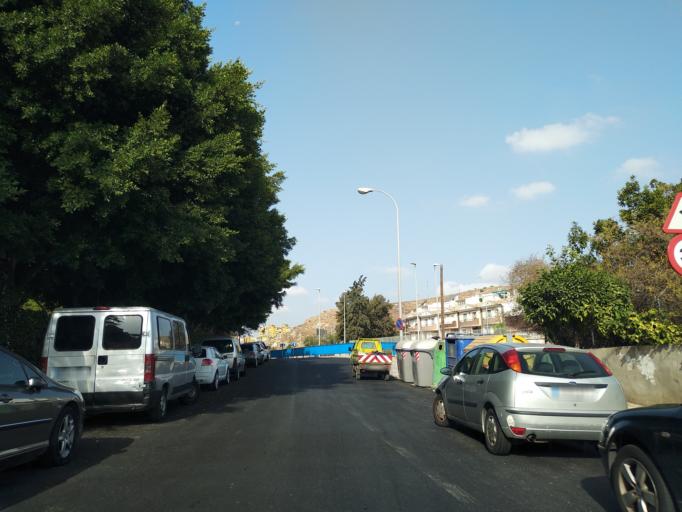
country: ES
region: Andalusia
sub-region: Provincia de Malaga
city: Malaga
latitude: 36.7263
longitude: -4.4502
